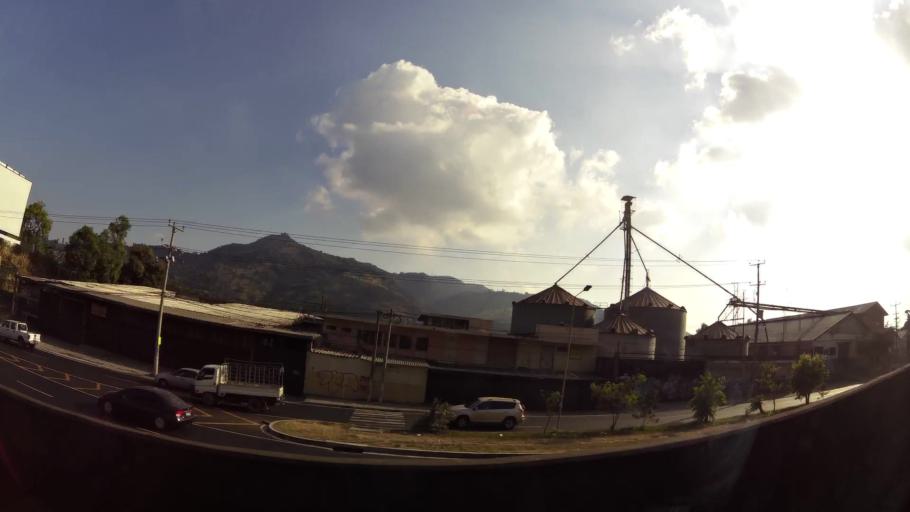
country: SV
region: San Salvador
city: San Salvador
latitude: 13.6999
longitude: -89.1725
